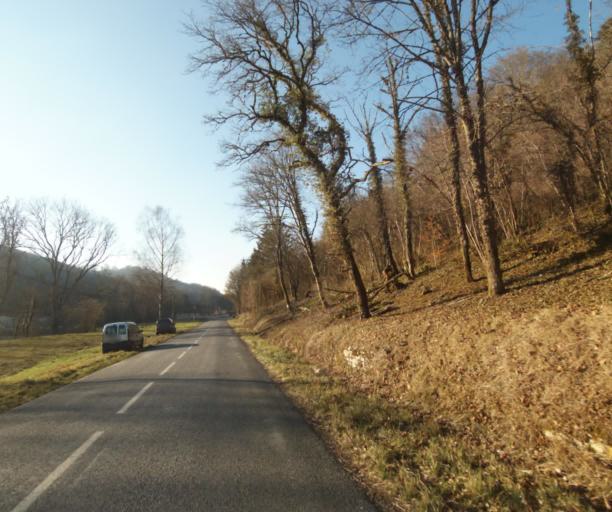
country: FR
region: Champagne-Ardenne
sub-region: Departement de la Haute-Marne
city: Chevillon
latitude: 48.5268
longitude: 5.1521
